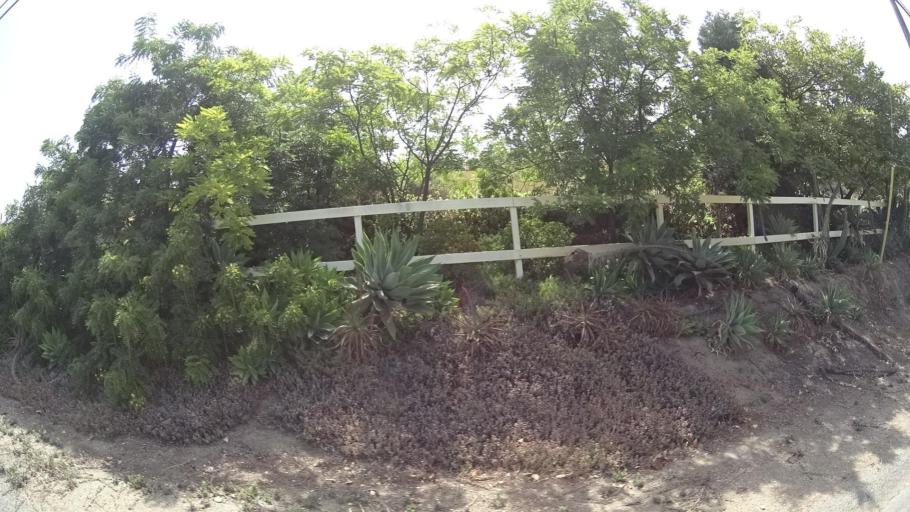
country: US
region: California
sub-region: San Diego County
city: Rainbow
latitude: 33.3924
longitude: -117.1714
